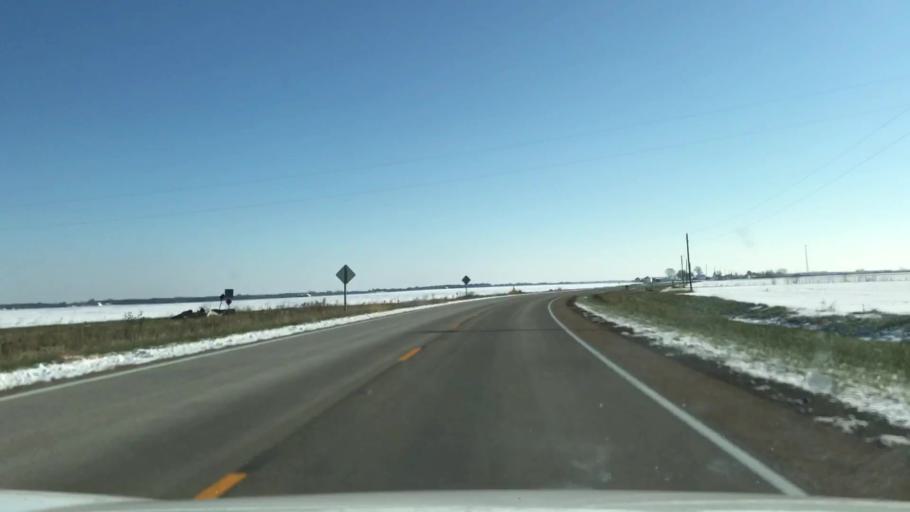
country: US
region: Illinois
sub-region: Washington County
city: Okawville
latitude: 38.4426
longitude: -89.5236
